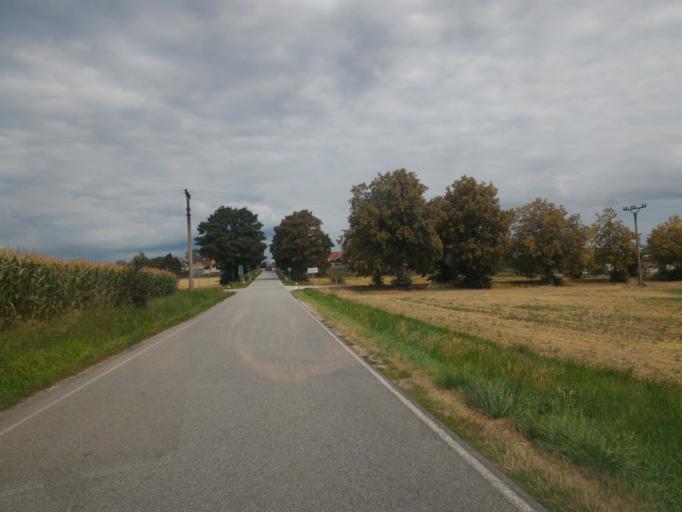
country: CZ
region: Jihocesky
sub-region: Okres Jindrichuv Hradec
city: Dacice
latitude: 49.1010
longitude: 15.4901
